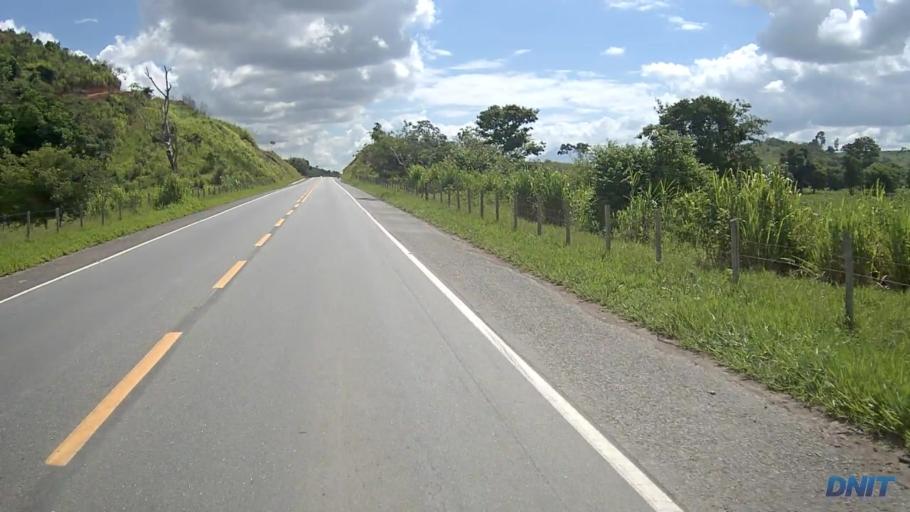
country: BR
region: Minas Gerais
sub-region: Governador Valadares
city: Governador Valadares
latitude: -18.9982
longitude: -42.1228
